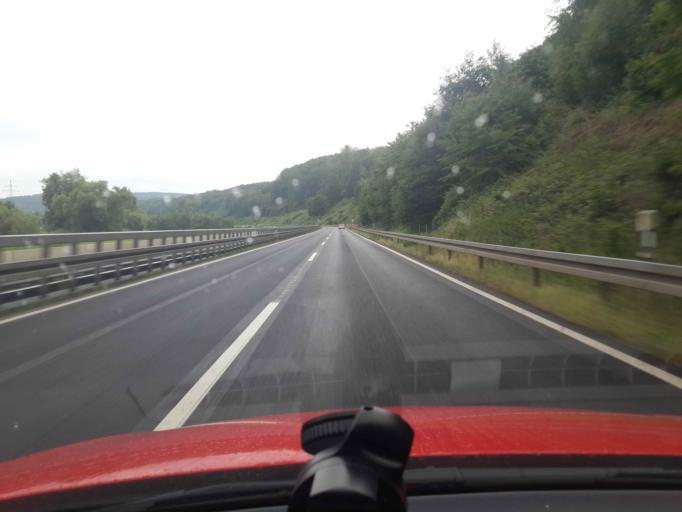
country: DE
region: Bavaria
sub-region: Regierungsbezirk Unterfranken
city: Obernburg am Main
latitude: 49.8213
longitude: 9.1358
